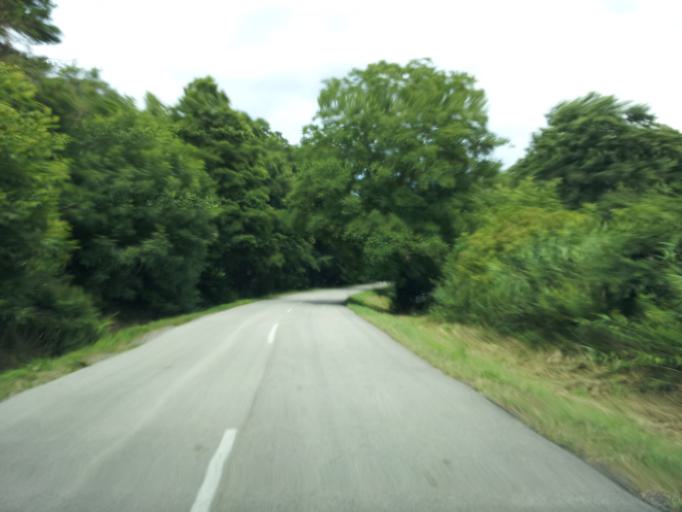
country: HU
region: Zala
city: Zalaszentgrot
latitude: 47.0155
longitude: 16.9708
